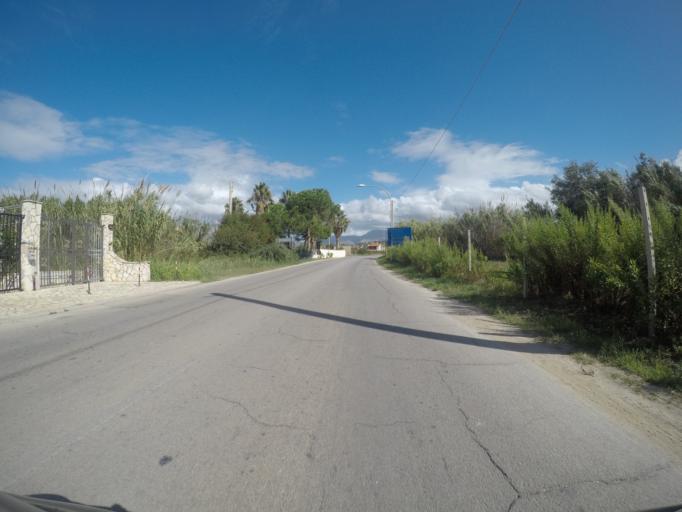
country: IT
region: Sicily
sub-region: Palermo
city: Trappeto
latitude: 38.0707
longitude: 13.0492
